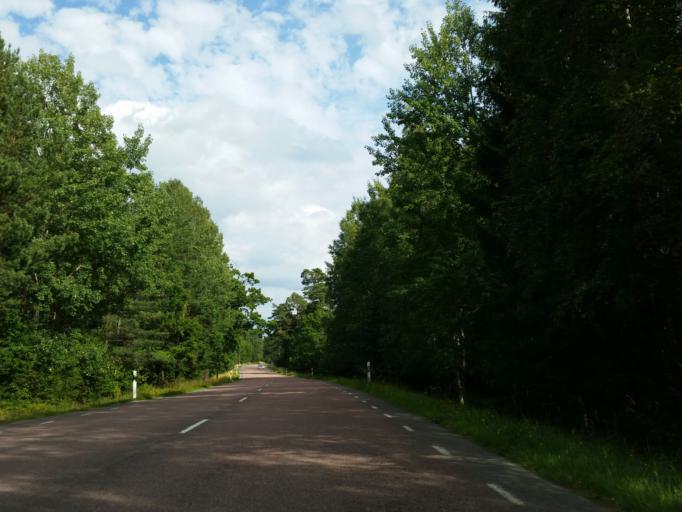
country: SE
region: Soedermanland
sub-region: Strangnas Kommun
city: Mariefred
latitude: 59.2218
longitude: 17.2697
